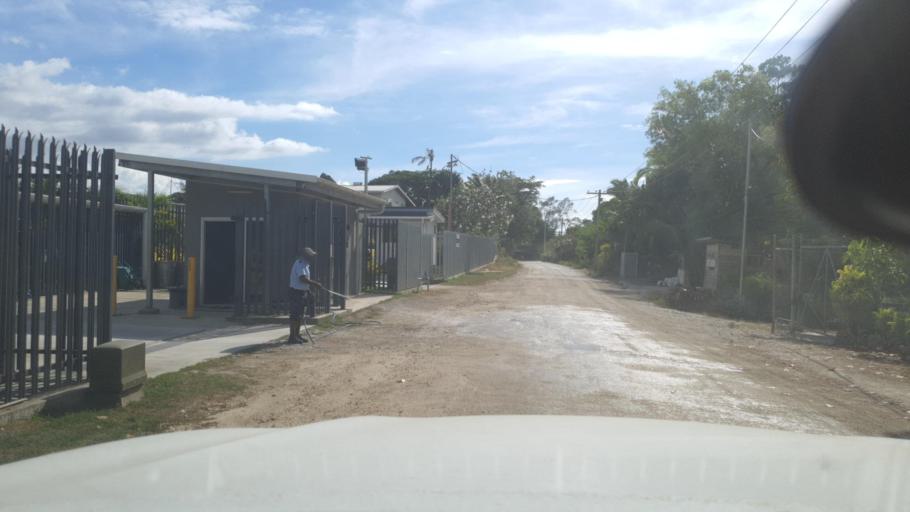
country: SB
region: Guadalcanal
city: Honiara
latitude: -9.4338
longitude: 159.9492
